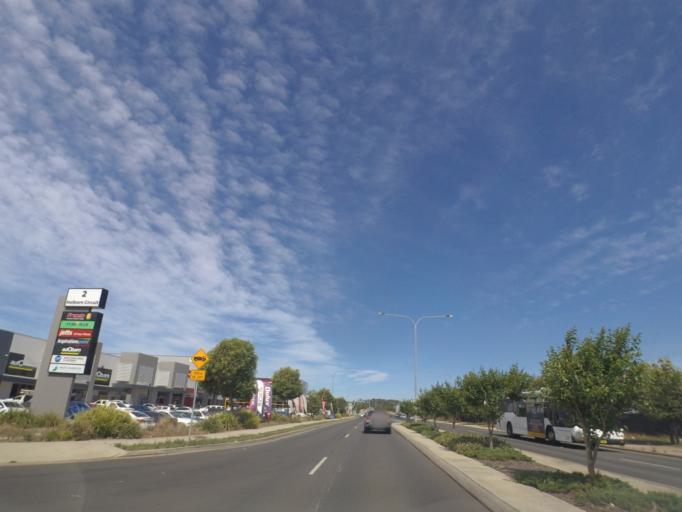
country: AU
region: New South Wales
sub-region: Camden
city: Narellan
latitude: -34.0212
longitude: 150.7637
